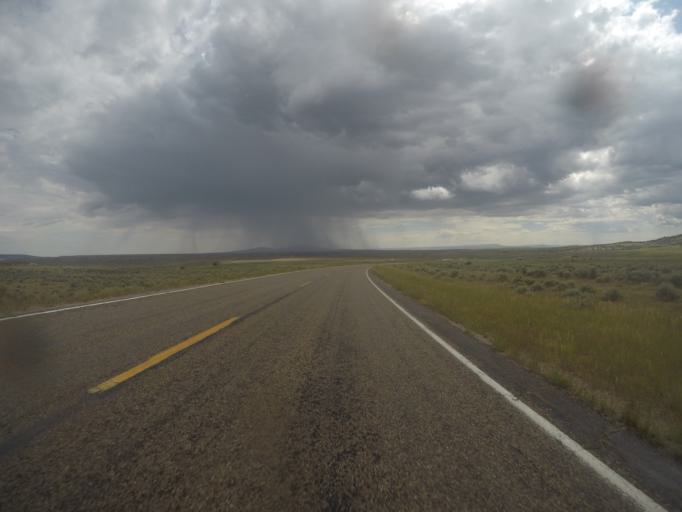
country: US
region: Utah
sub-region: Daggett County
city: Manila
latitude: 41.0251
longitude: -109.8905
